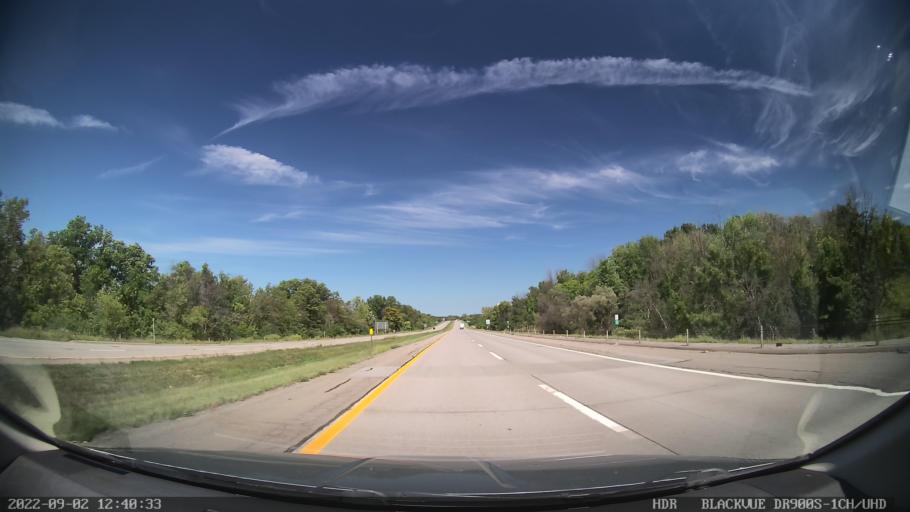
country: US
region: New York
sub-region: Livingston County
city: Mount Morris
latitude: 42.7393
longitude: -77.8396
